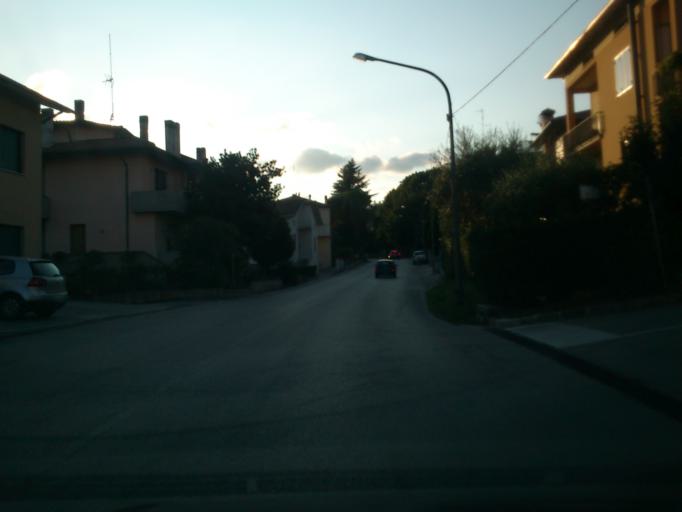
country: IT
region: The Marches
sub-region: Provincia di Pesaro e Urbino
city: Calcinelli
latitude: 43.7522
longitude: 12.9141
